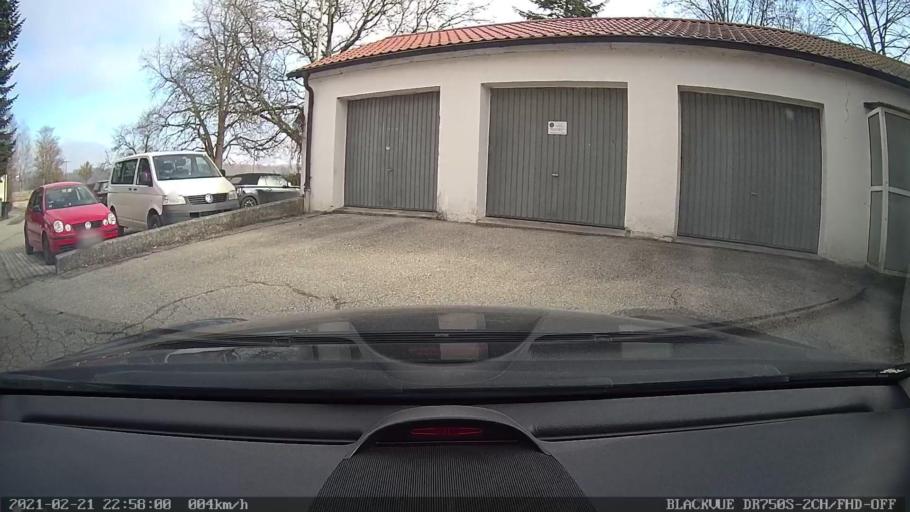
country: DE
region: Bavaria
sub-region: Upper Bavaria
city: Griesstatt
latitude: 48.0088
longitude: 12.1776
